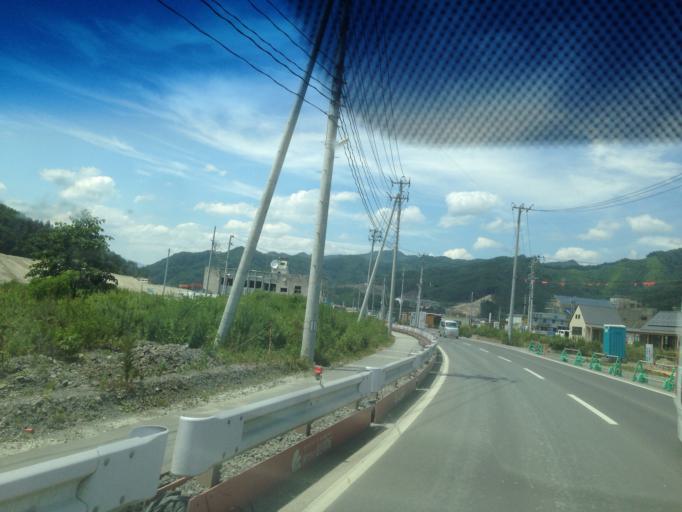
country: JP
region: Iwate
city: Otsuchi
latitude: 39.3584
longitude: 141.9078
